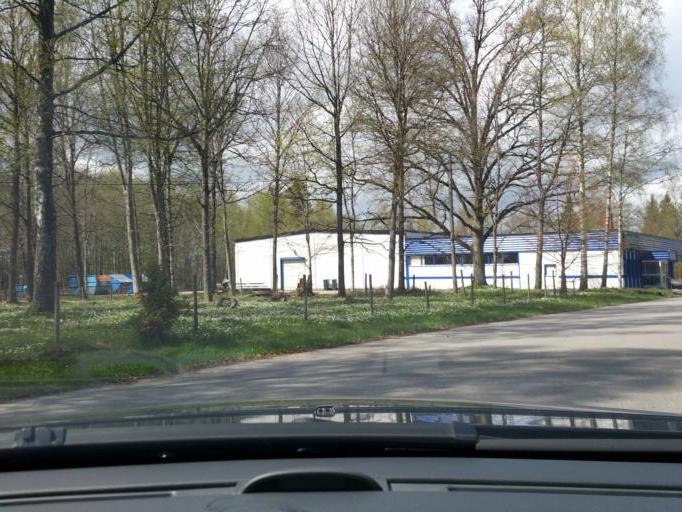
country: SE
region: Kronoberg
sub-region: Vaxjo Kommun
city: Lammhult
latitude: 57.1589
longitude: 14.5877
